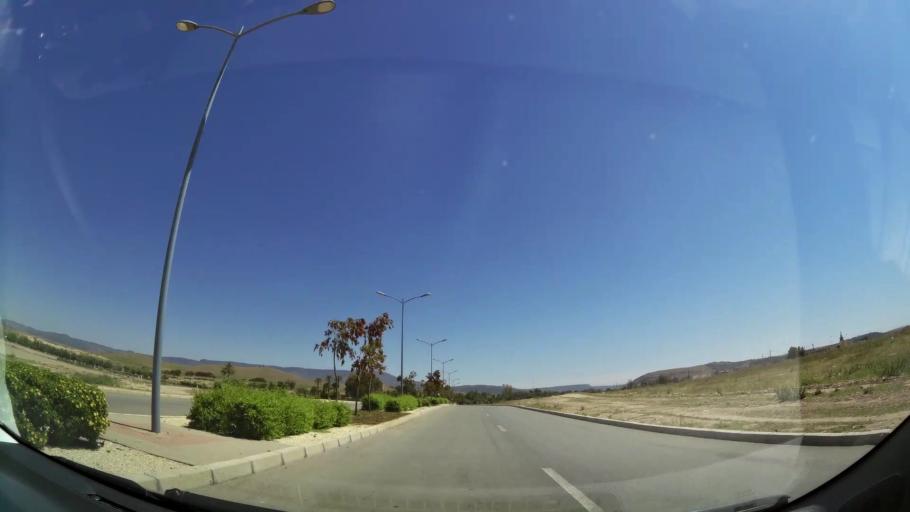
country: MA
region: Oriental
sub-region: Oujda-Angad
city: Oujda
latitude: 34.6704
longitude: -1.8652
